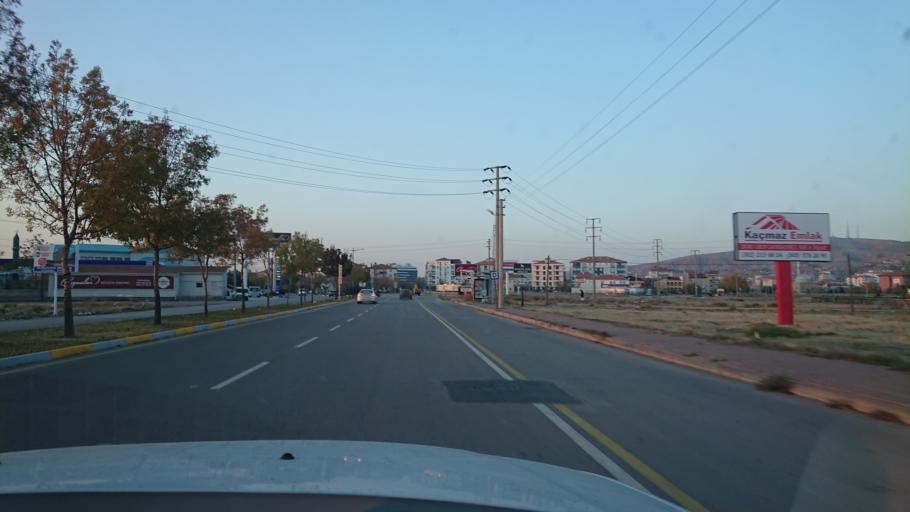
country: TR
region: Aksaray
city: Aksaray
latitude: 38.3509
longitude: 34.0432
